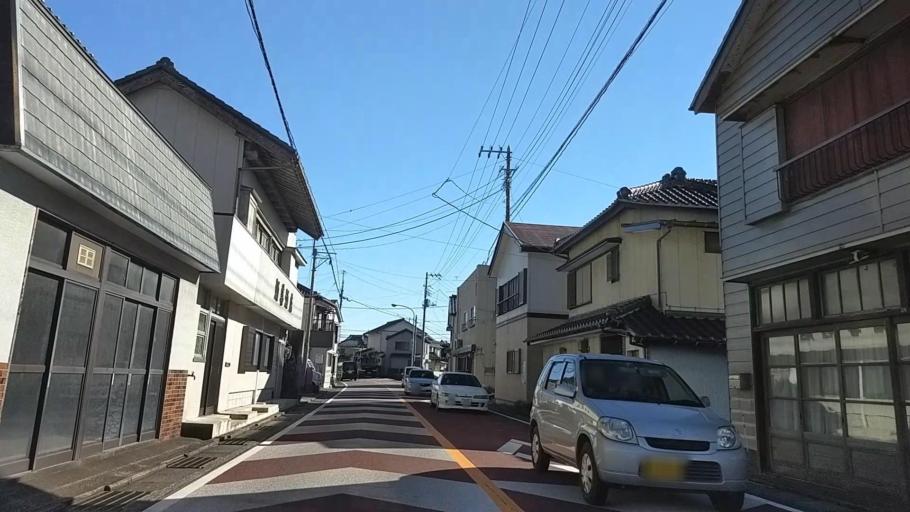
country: JP
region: Chiba
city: Kawaguchi
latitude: 35.0369
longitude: 140.0144
